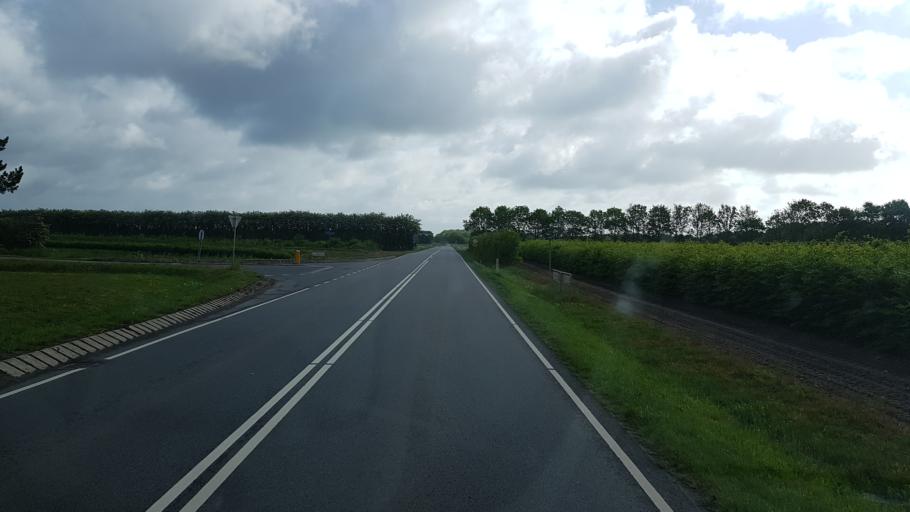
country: DK
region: South Denmark
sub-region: Vejen Kommune
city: Vejen
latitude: 55.4551
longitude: 9.1576
